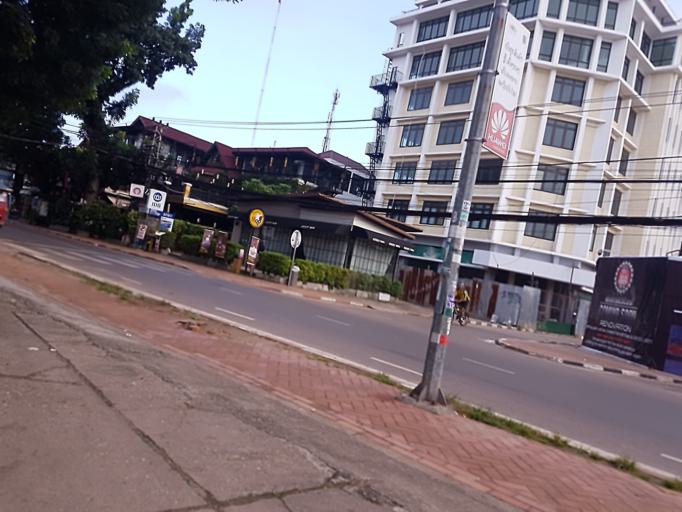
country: LA
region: Vientiane
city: Vientiane
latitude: 17.9643
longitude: 102.6076
